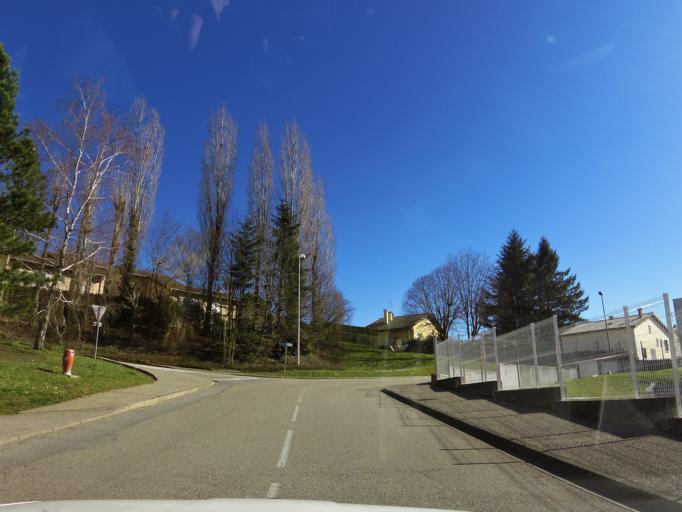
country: FR
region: Rhone-Alpes
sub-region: Departement de l'Ain
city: Amberieu-en-Bugey
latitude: 45.9611
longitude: 5.3598
